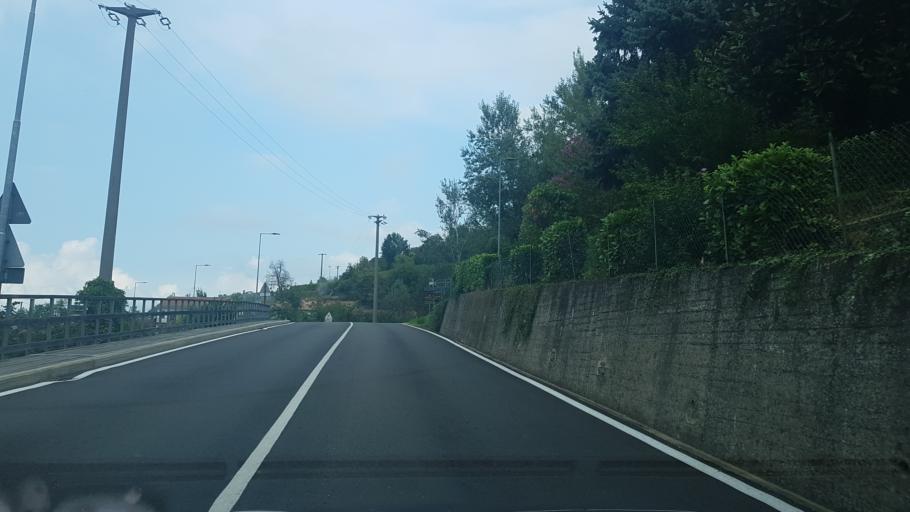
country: IT
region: Piedmont
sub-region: Provincia di Cuneo
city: Cossano Belbo
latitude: 44.6632
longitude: 8.1950
